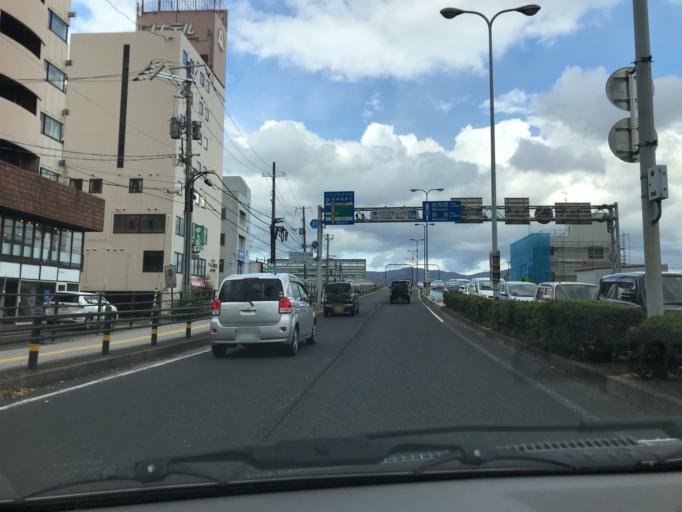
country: JP
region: Shimane
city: Matsue-shi
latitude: 35.4649
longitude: 133.0651
